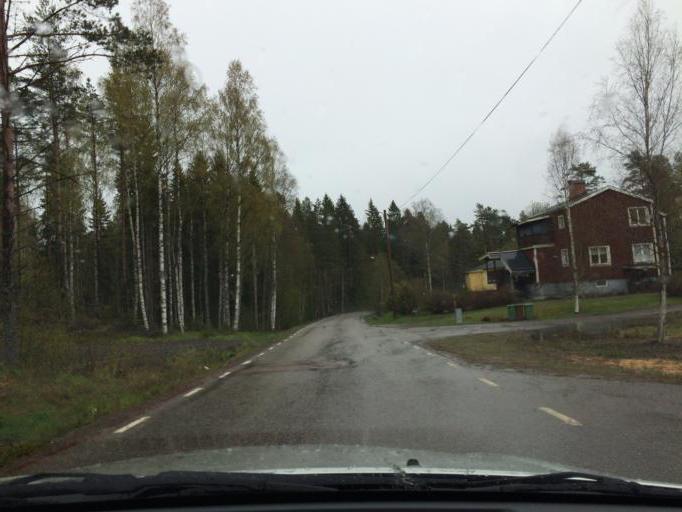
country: SE
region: Dalarna
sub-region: Ludvika Kommun
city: Abborrberget
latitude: 60.0452
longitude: 14.7589
